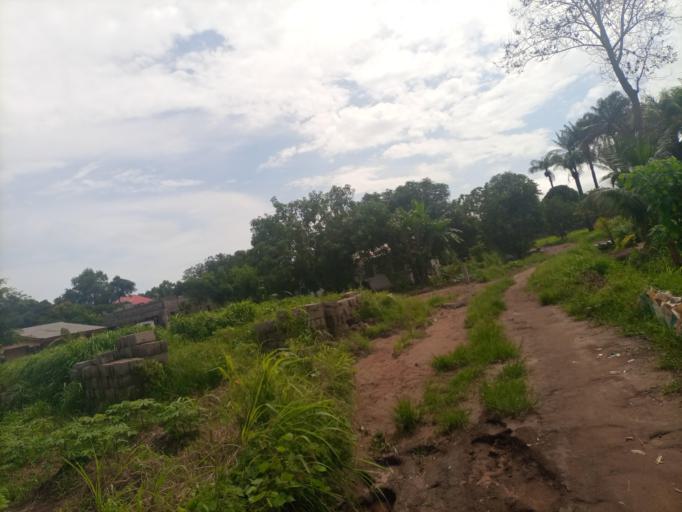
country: SL
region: Northern Province
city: Sawkta
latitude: 8.6354
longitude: -13.2084
